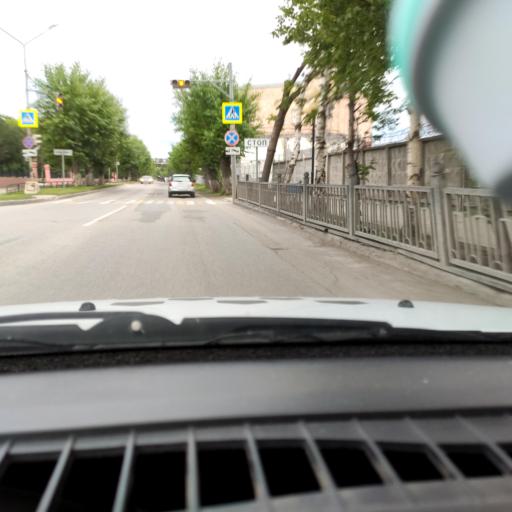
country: RU
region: Perm
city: Chusovoy
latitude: 58.2949
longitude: 57.8136
